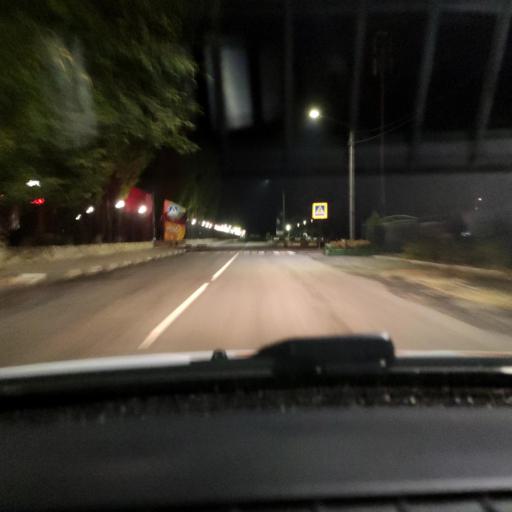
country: RU
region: Voronezj
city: Voronezh
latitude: 51.6304
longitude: 39.1659
